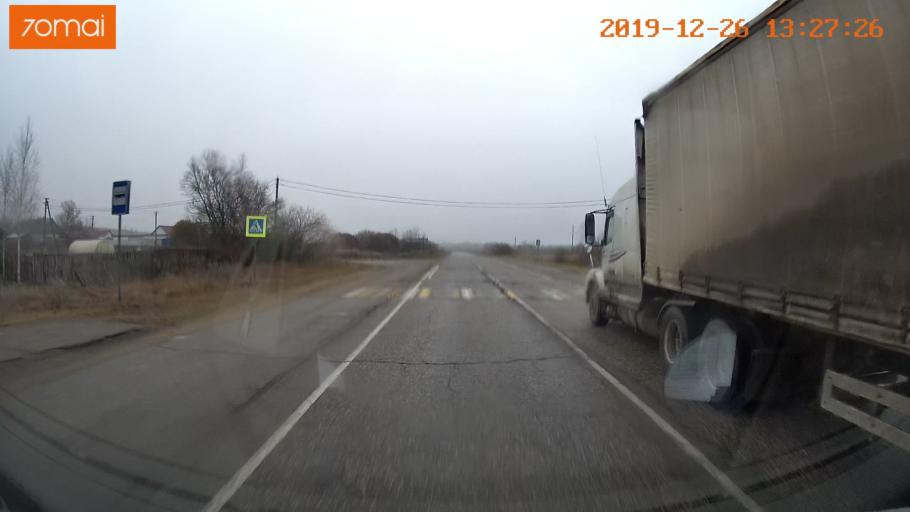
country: RU
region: Vologda
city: Cherepovets
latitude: 58.8538
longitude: 38.2399
